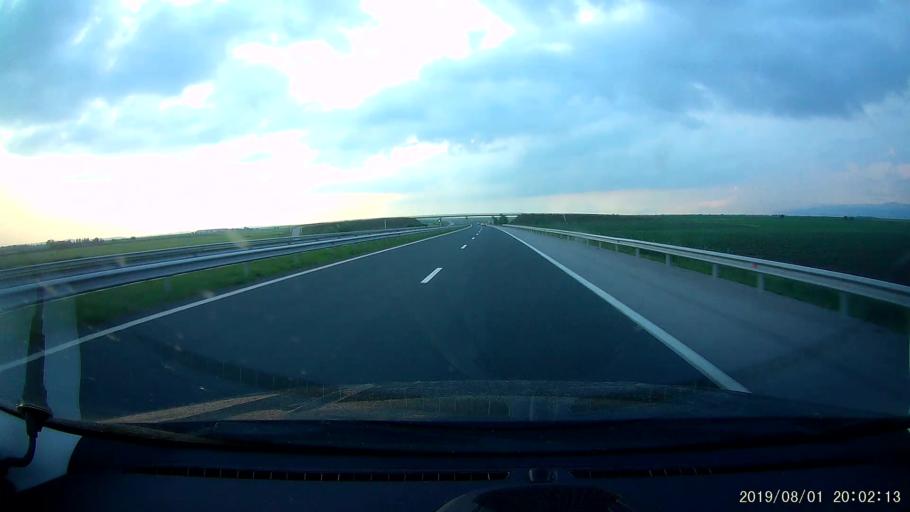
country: BG
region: Yambol
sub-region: Obshtina Straldzha
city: Straldzha
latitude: 42.5589
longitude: 26.6375
